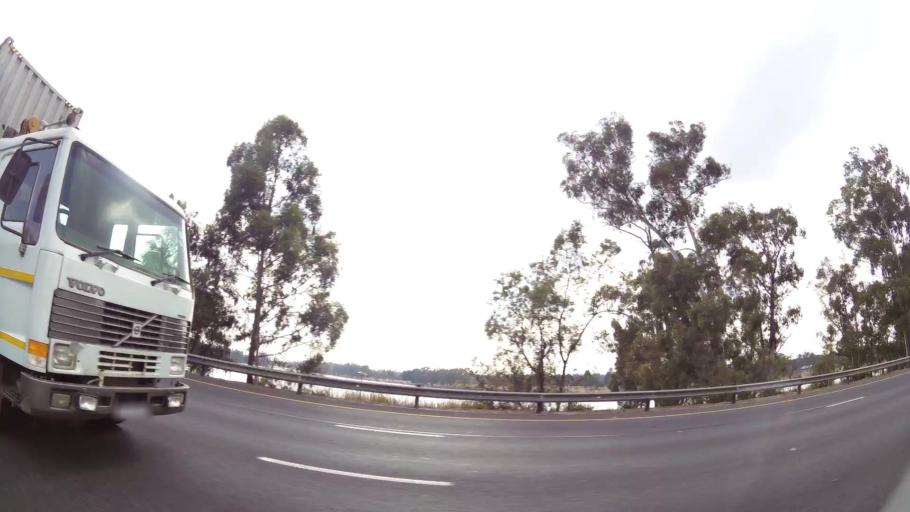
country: ZA
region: Gauteng
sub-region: Ekurhuleni Metropolitan Municipality
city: Benoni
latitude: -26.1748
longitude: 28.2882
